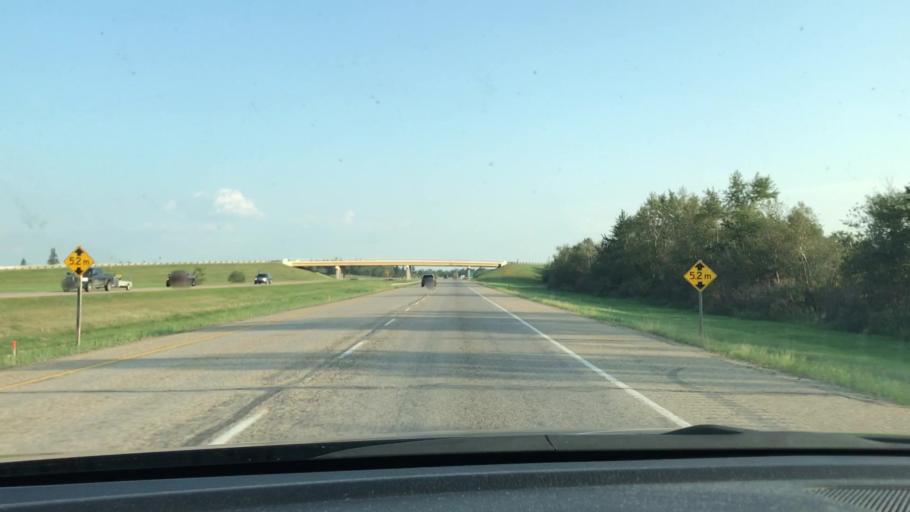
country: CA
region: Alberta
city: Lacombe
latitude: 52.5621
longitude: -113.6630
